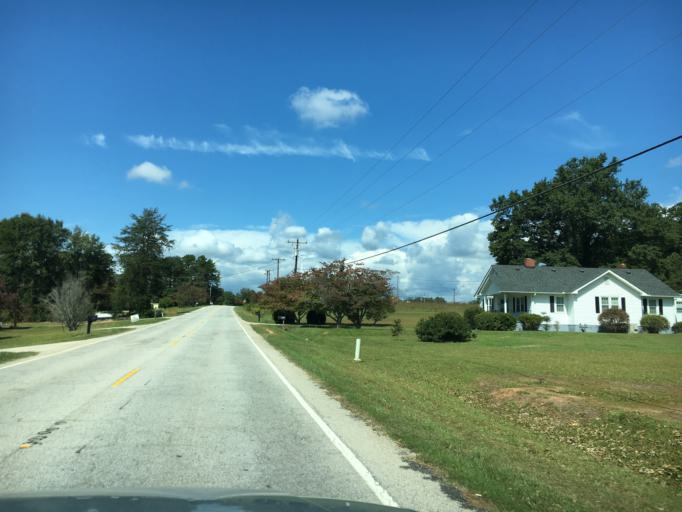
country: US
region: South Carolina
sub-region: Greenville County
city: Tigerville
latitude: 35.0142
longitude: -82.3773
